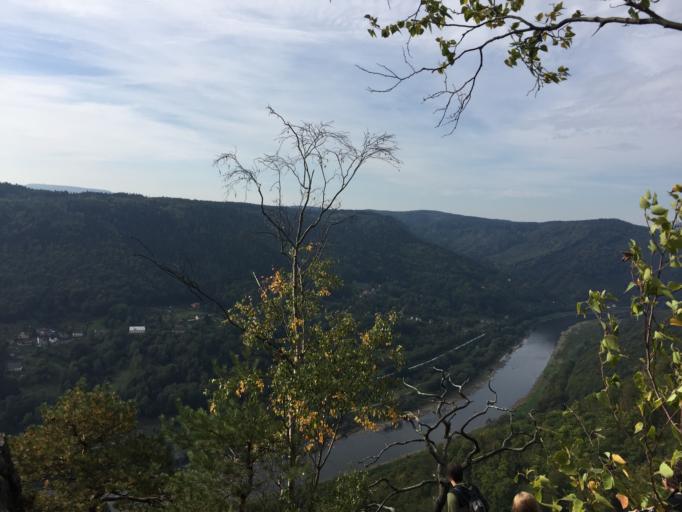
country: CZ
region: Ustecky
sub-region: Okres Decin
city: Decin
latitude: 50.8021
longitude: 14.2447
